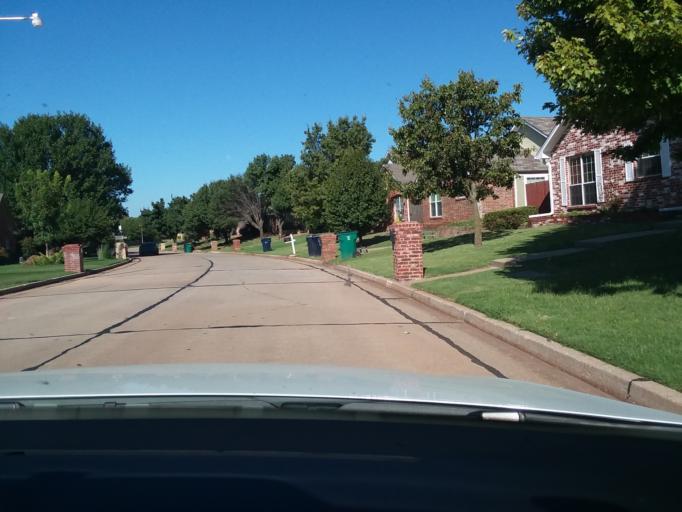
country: US
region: Oklahoma
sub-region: Oklahoma County
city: The Village
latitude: 35.6016
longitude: -97.5636
